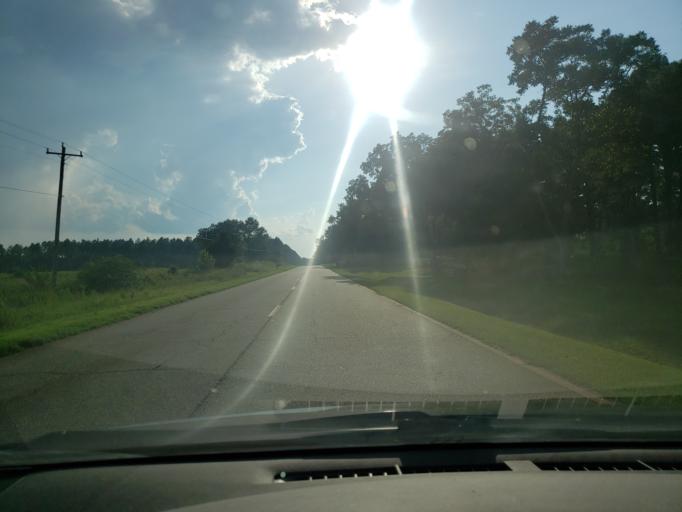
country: US
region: Georgia
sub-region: Dougherty County
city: Albany
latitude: 31.5734
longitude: -84.3212
